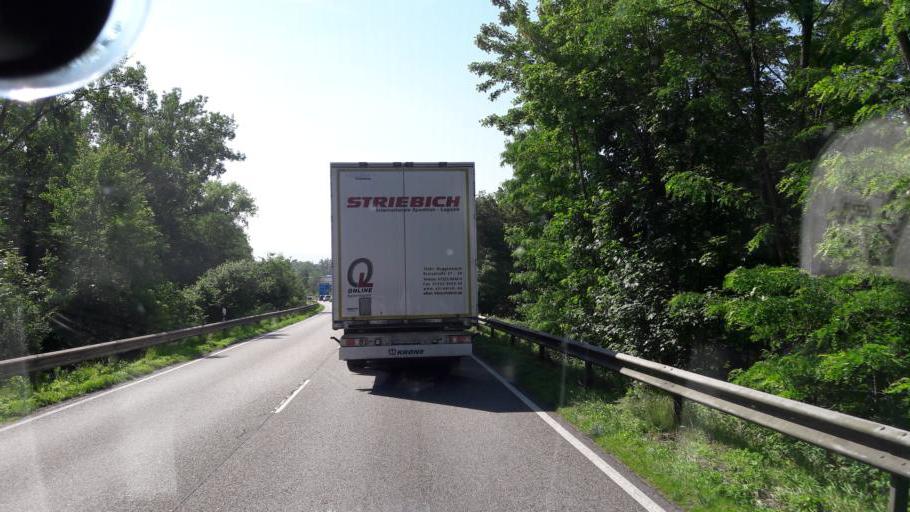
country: DE
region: Baden-Wuerttemberg
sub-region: Karlsruhe Region
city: Otigheim
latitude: 48.8669
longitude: 8.2364
